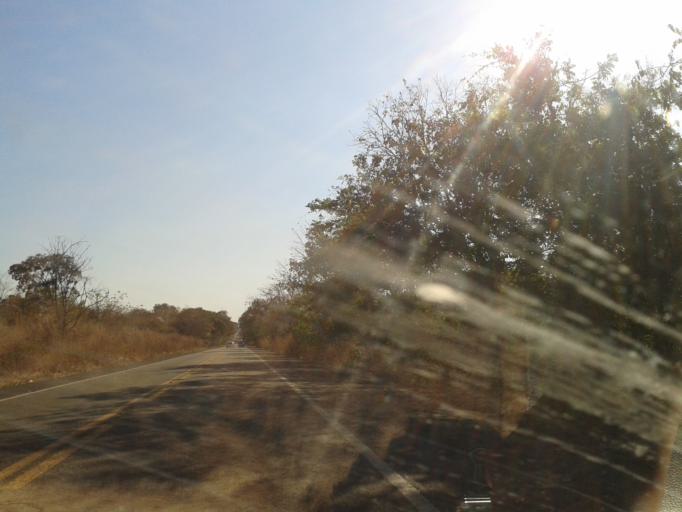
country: BR
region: Goias
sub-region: Mozarlandia
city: Mozarlandia
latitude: -15.0410
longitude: -50.6051
